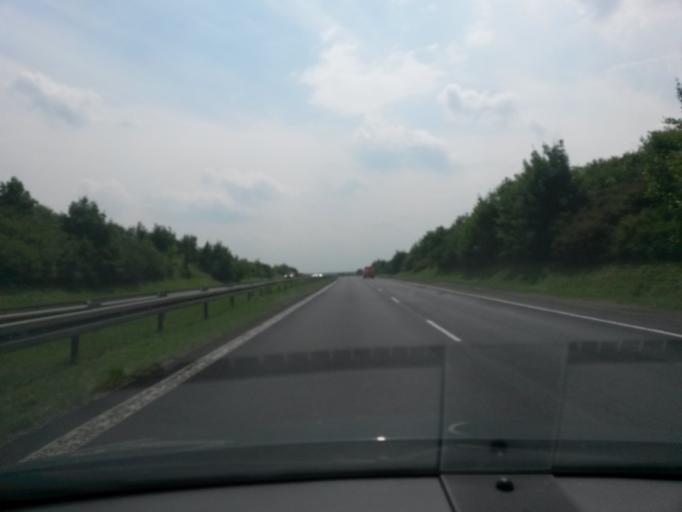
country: PL
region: Lodz Voivodeship
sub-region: Powiat radomszczanski
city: Kamiensk
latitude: 51.1936
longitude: 19.4737
